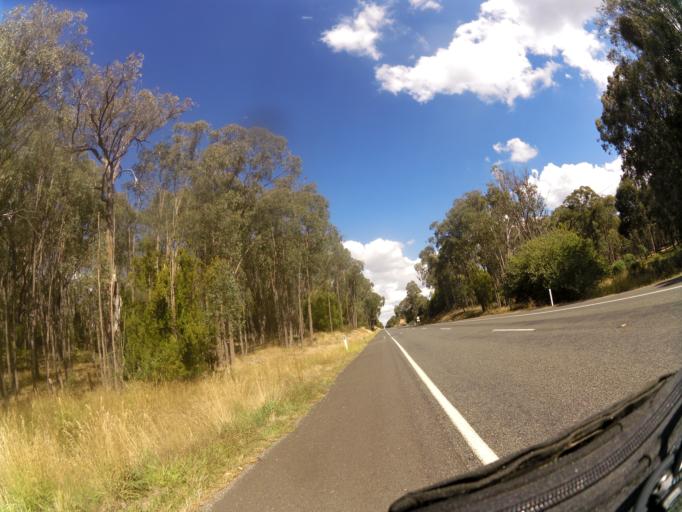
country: AU
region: Victoria
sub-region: Mansfield
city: Mansfield
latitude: -36.8784
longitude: 145.9936
